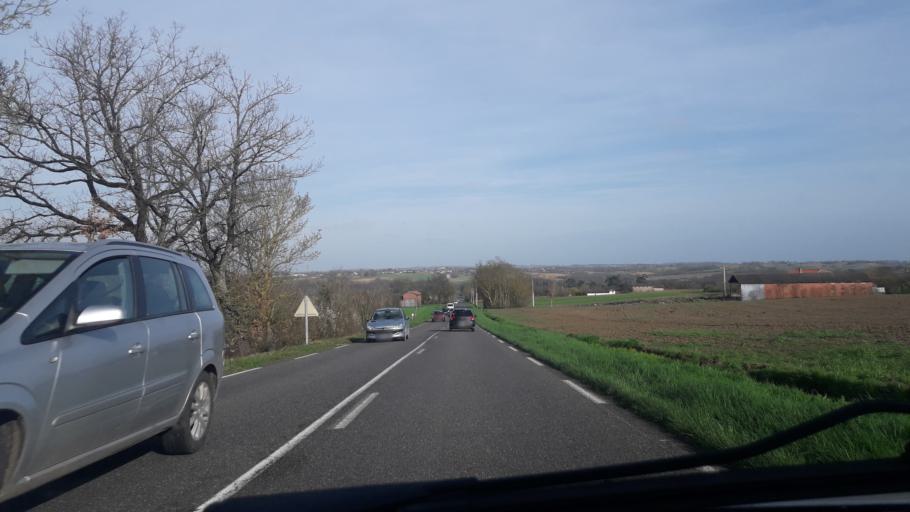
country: FR
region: Midi-Pyrenees
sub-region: Departement du Gers
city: Gimont
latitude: 43.7202
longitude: 0.9397
